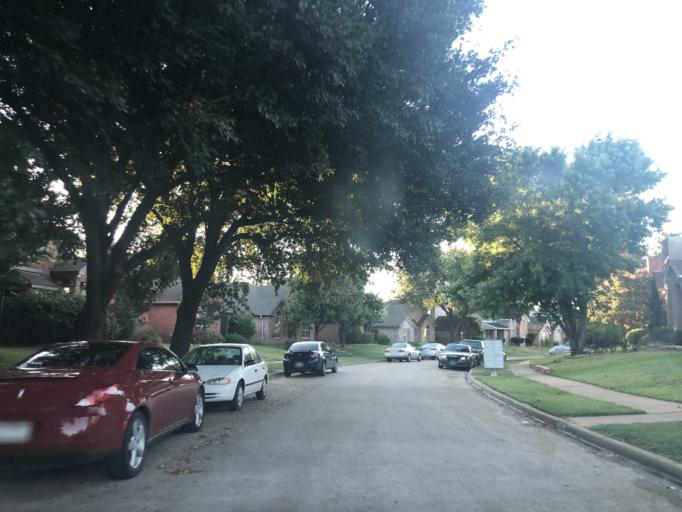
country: US
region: Texas
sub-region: Dallas County
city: Grand Prairie
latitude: 32.6689
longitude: -96.9946
